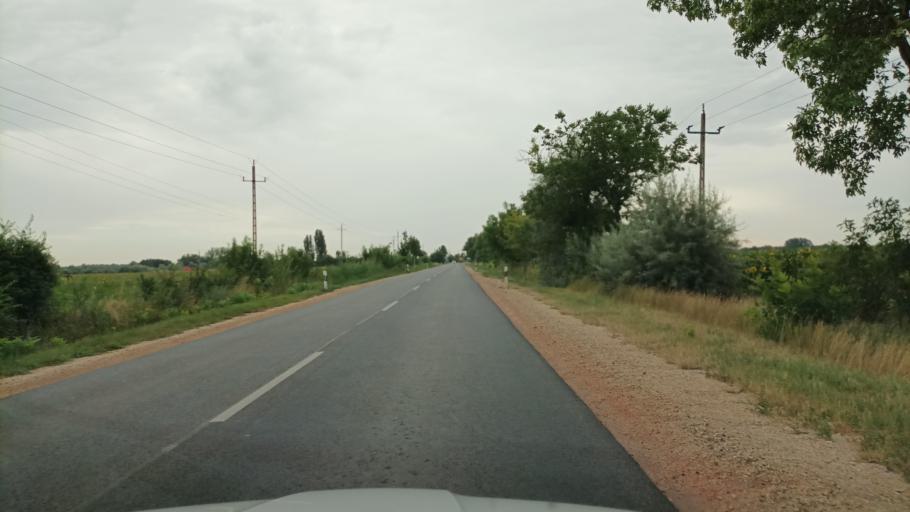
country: HU
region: Pest
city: Bugyi
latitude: 47.2383
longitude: 19.1892
